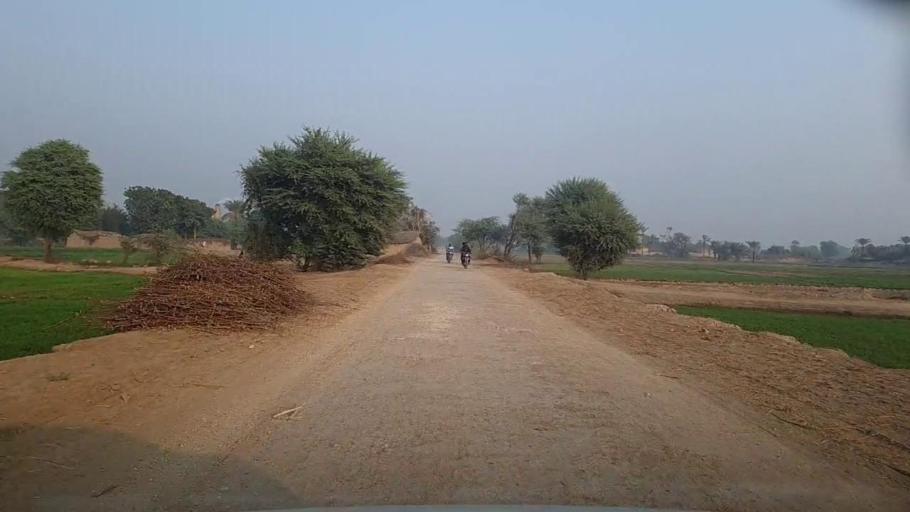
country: PK
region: Sindh
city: Bozdar
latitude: 27.0831
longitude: 68.5516
